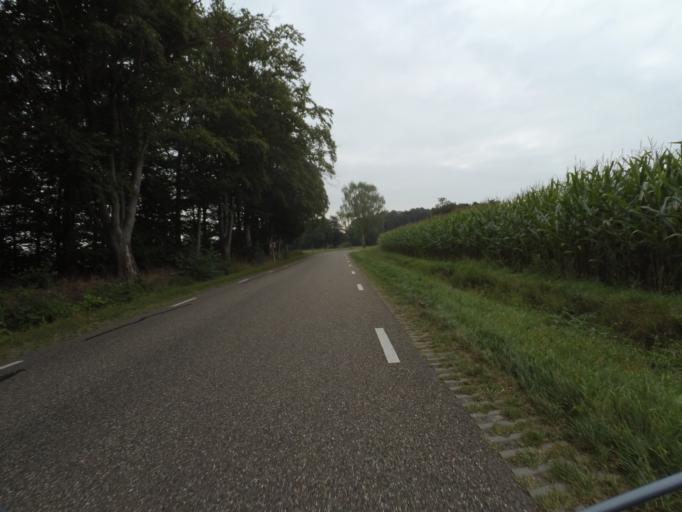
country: NL
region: Overijssel
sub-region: Gemeente Losser
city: Losser
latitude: 52.2956
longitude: 7.0188
